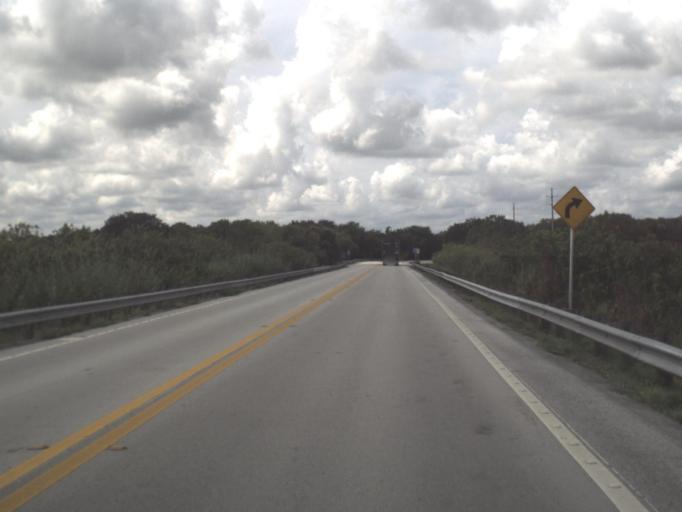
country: US
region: Florida
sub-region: Glades County
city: Buckhead Ridge
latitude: 27.2377
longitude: -80.9854
